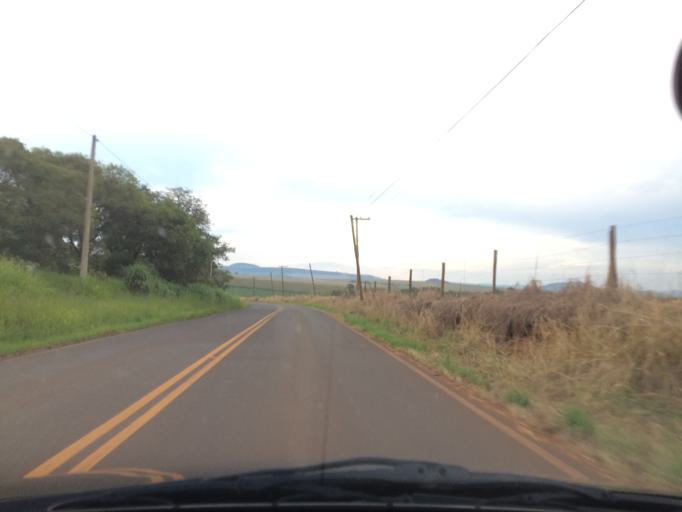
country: BR
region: Sao Paulo
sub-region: Casa Branca
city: Casa Branca
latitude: -21.7496
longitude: -47.1382
